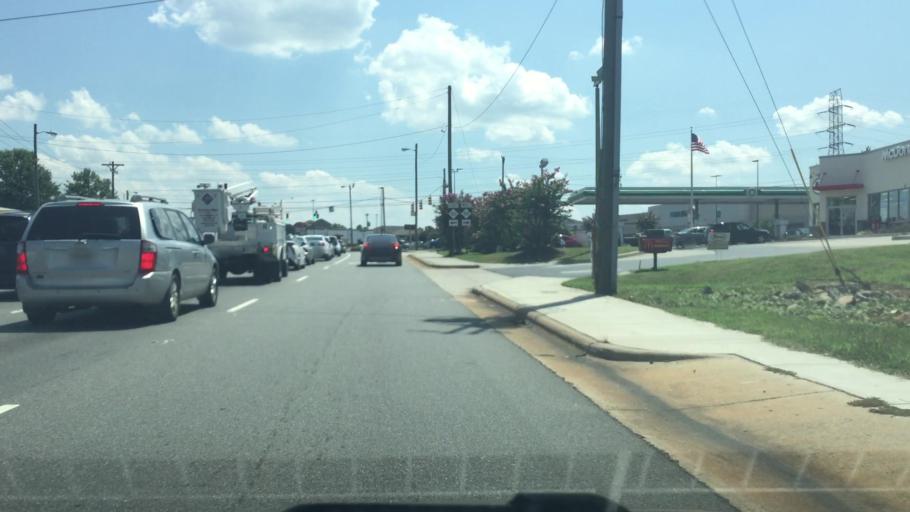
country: US
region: North Carolina
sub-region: Rowan County
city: Salisbury
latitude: 35.6631
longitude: -80.5002
